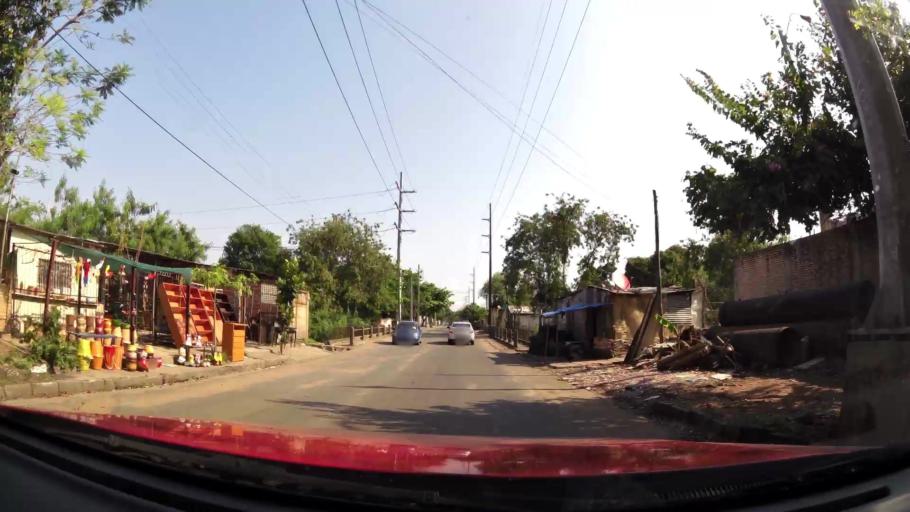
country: PY
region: Asuncion
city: Asuncion
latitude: -25.3137
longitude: -57.6335
